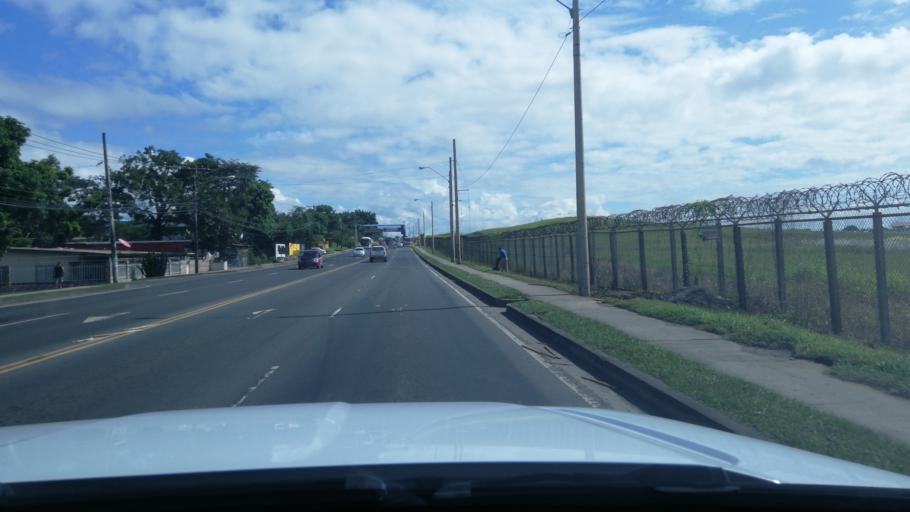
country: PA
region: Panama
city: Tocumen
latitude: 9.0896
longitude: -79.3811
